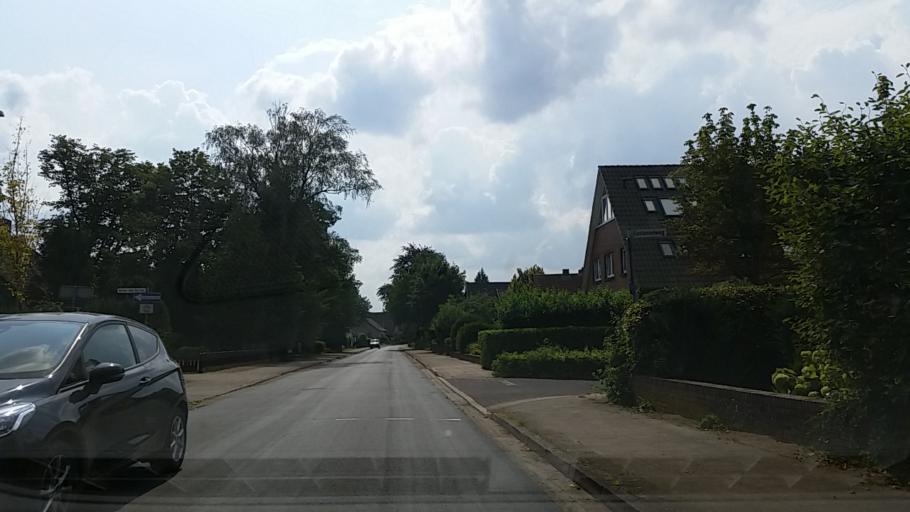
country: DE
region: Lower Saxony
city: Schneverdingen
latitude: 53.1236
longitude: 9.7855
